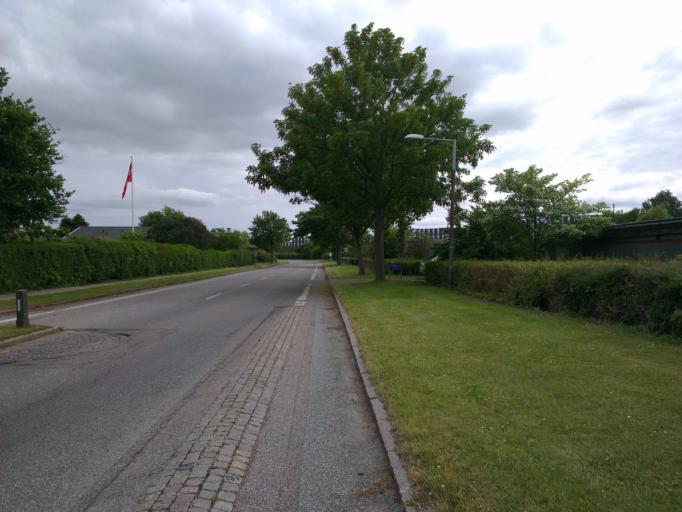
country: DK
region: Capital Region
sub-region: Frederikssund Kommune
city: Frederikssund
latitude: 55.8520
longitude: 12.0570
